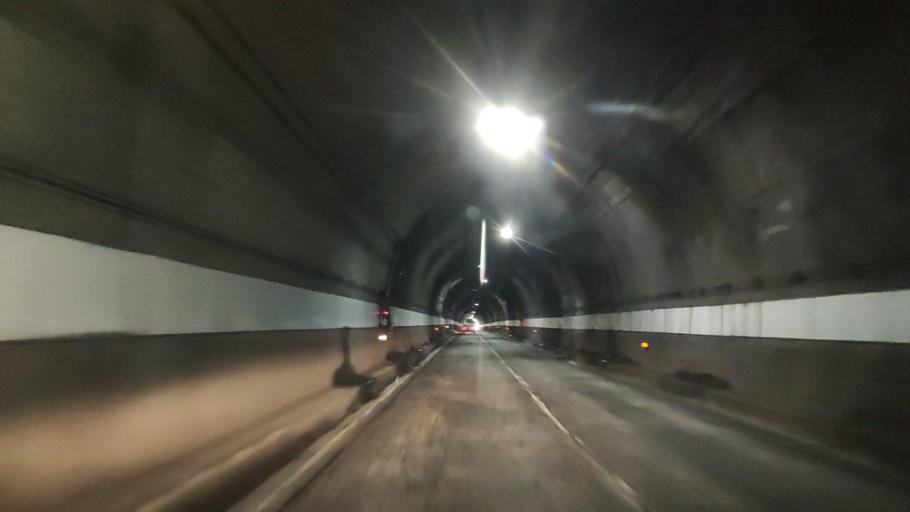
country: JP
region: Nagano
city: Toyoshina
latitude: 36.1359
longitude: 137.7123
